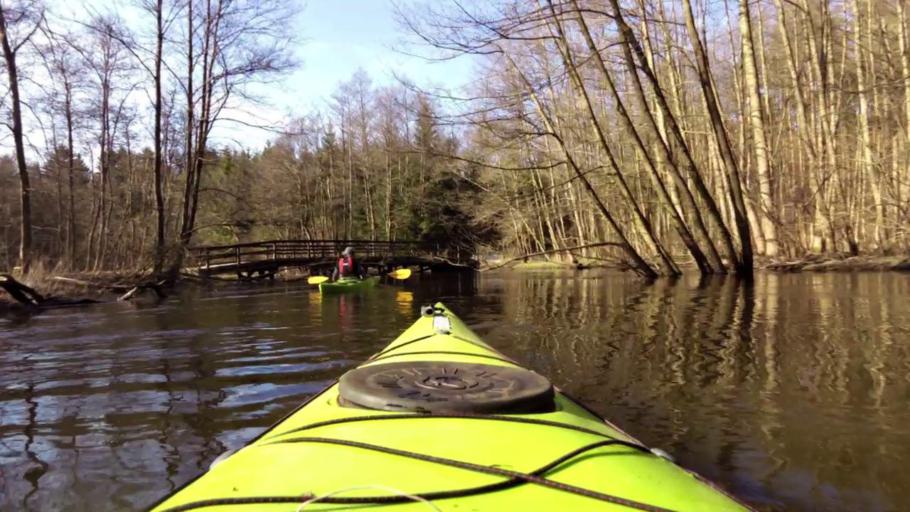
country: PL
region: West Pomeranian Voivodeship
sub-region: Powiat lobeski
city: Lobez
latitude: 53.7089
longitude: 15.5484
